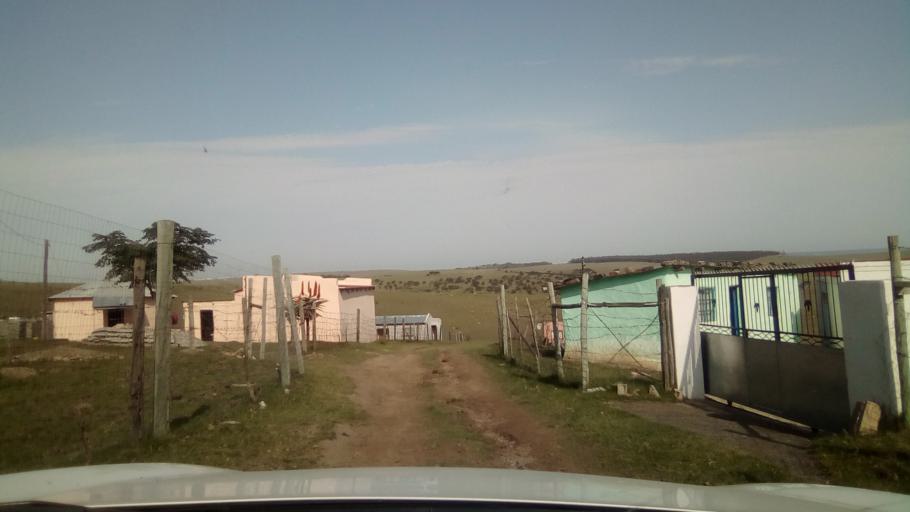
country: ZA
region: Eastern Cape
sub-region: Buffalo City Metropolitan Municipality
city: Bhisho
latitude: -32.9884
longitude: 27.2705
